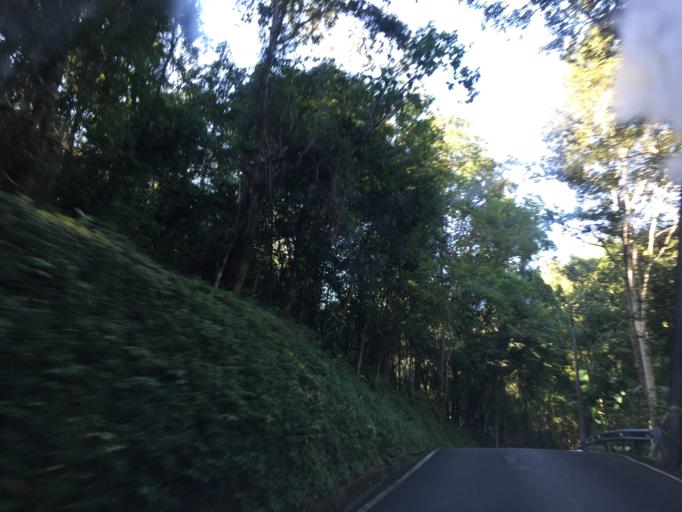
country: TH
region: Chiang Mai
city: Chiang Mai
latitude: 18.8036
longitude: 98.9424
